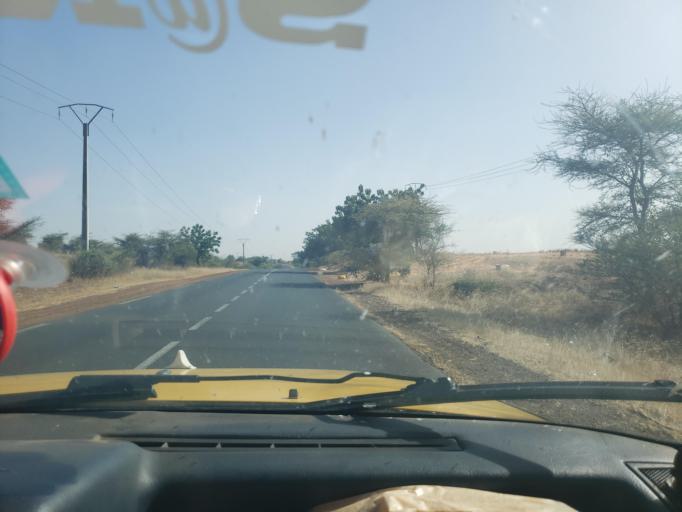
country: SN
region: Louga
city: Louga
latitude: 15.6511
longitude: -16.2551
